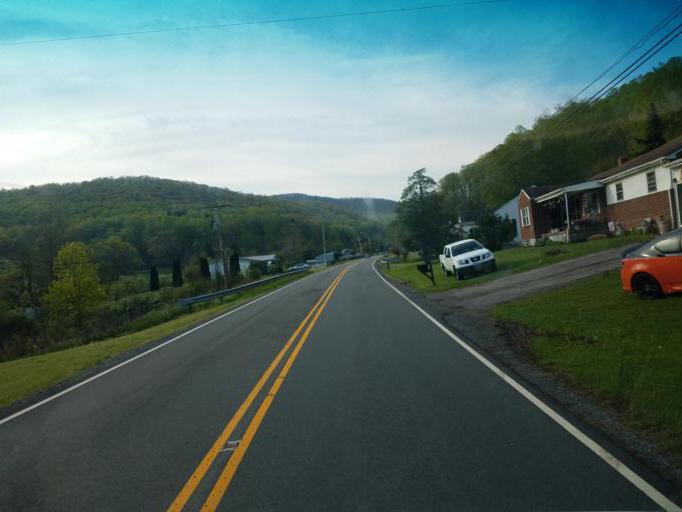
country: US
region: Virginia
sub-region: Smyth County
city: Marion
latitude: 36.8208
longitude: -81.4718
